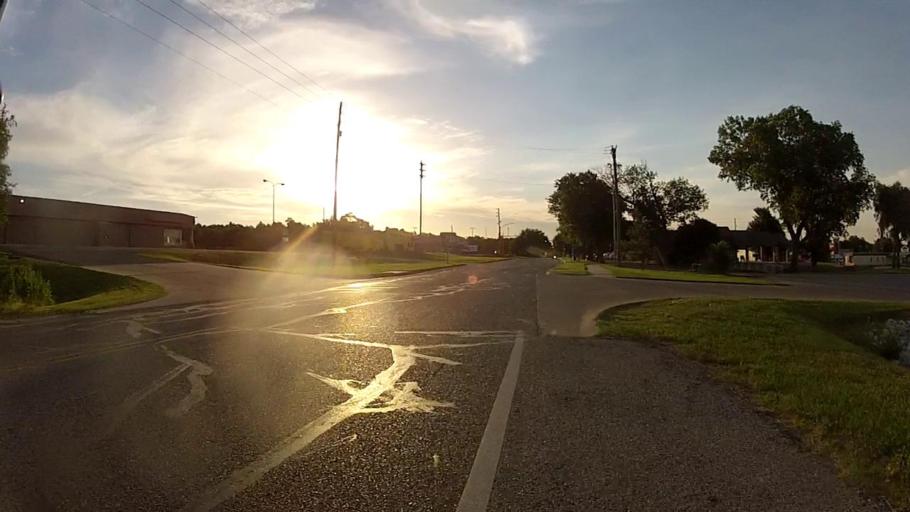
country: US
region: Kansas
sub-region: Cowley County
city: Arkansas City
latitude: 37.0854
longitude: -97.0418
